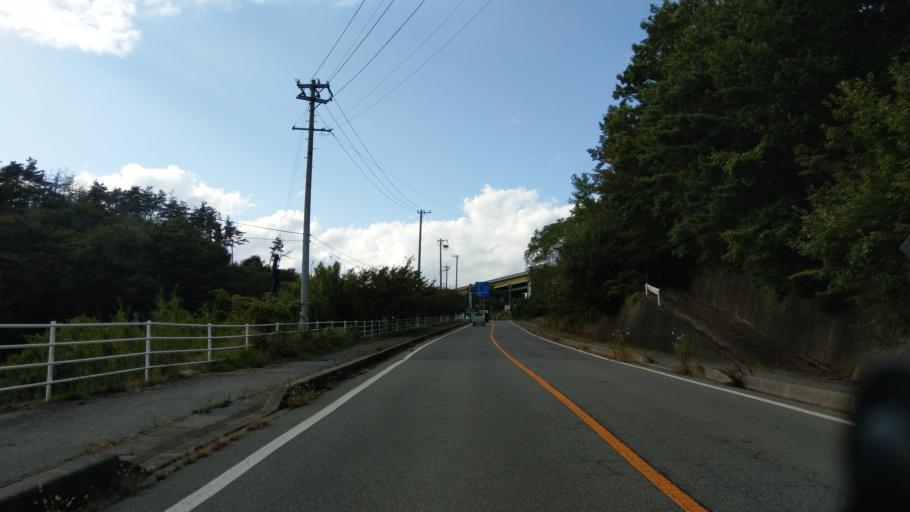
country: JP
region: Nagano
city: Komoro
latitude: 36.3437
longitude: 138.4160
